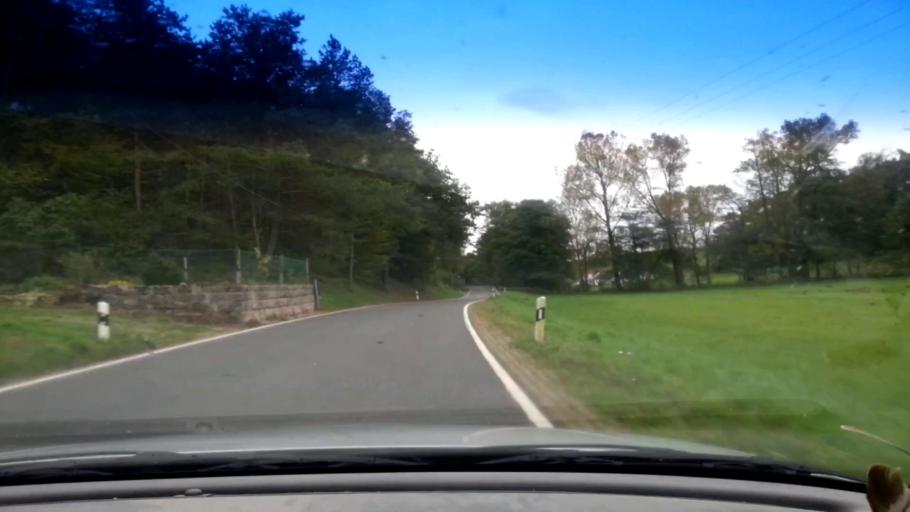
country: DE
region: Bavaria
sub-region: Upper Franconia
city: Lauter
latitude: 49.9851
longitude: 10.7649
